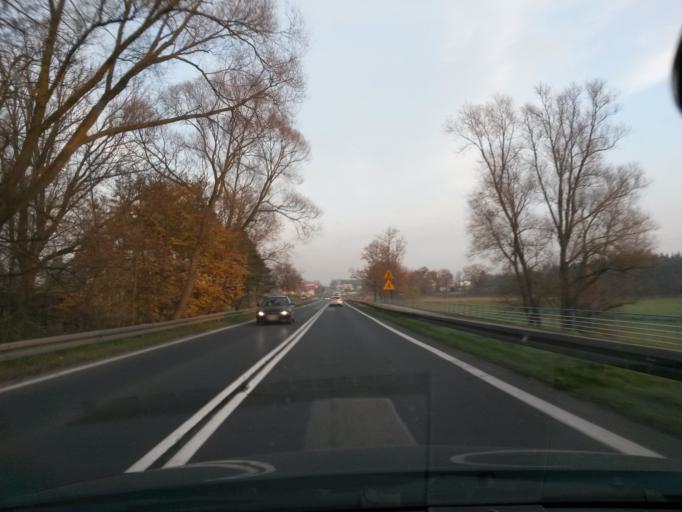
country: PL
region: Lodz Voivodeship
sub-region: Powiat wielunski
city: Osjakow
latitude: 51.2822
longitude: 18.7821
